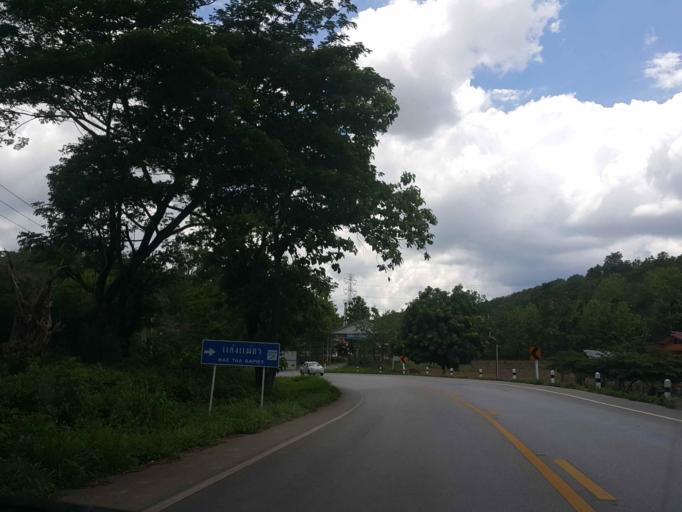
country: TH
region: Nan
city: Wiang Sa
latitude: 18.5232
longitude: 100.5565
